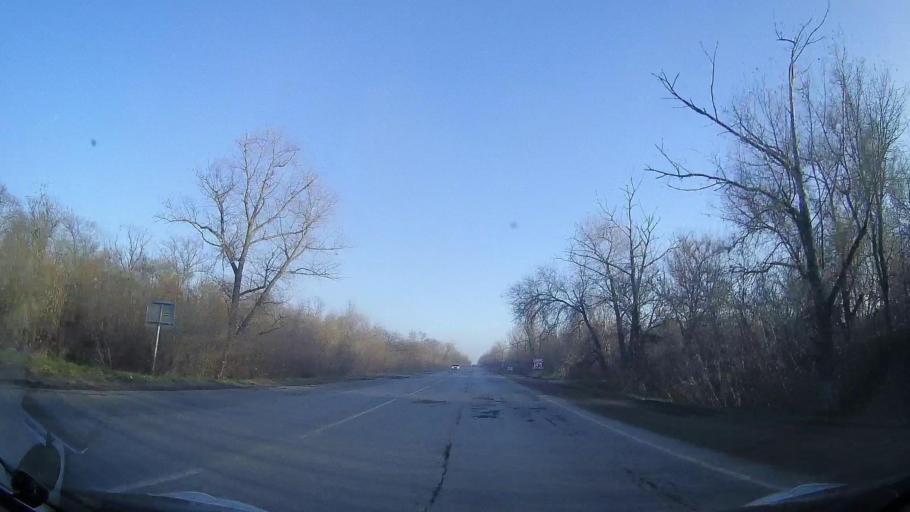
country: RU
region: Rostov
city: Bataysk
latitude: 47.0458
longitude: 39.8474
